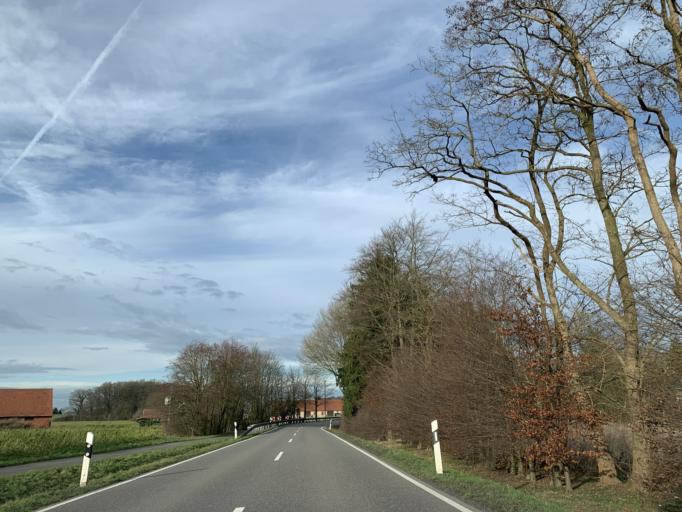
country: DE
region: North Rhine-Westphalia
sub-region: Regierungsbezirk Munster
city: Billerbeck
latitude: 51.9545
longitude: 7.3200
